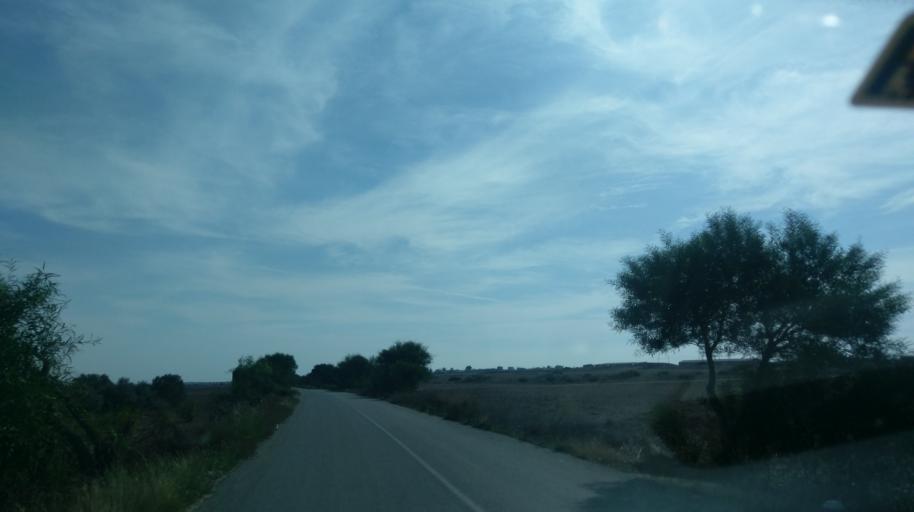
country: CY
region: Ammochostos
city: Lefkonoiko
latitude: 35.2298
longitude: 33.6892
